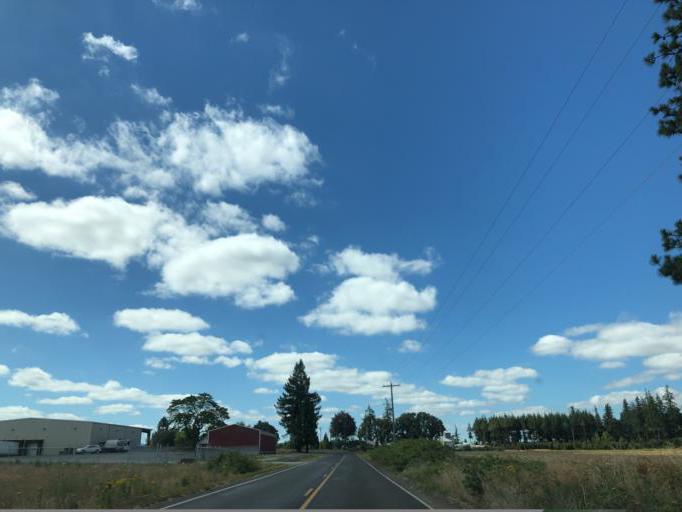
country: US
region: Oregon
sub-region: Marion County
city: Mount Angel
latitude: 45.1285
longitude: -122.7326
